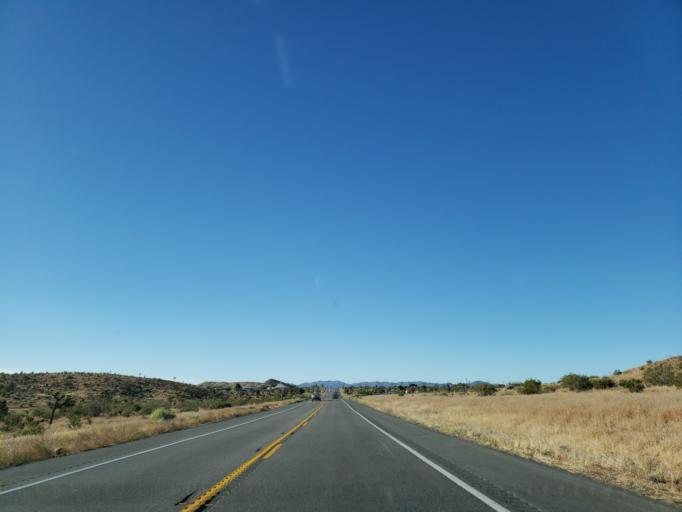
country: US
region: California
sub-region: San Bernardino County
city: Yucca Valley
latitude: 34.1828
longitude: -116.4298
